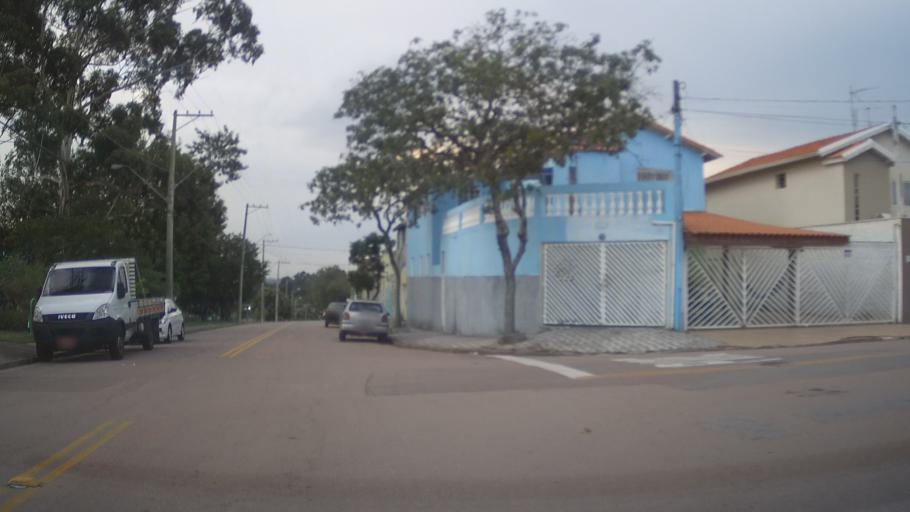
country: BR
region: Sao Paulo
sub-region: Jundiai
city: Jundiai
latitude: -23.1868
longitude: -46.9658
